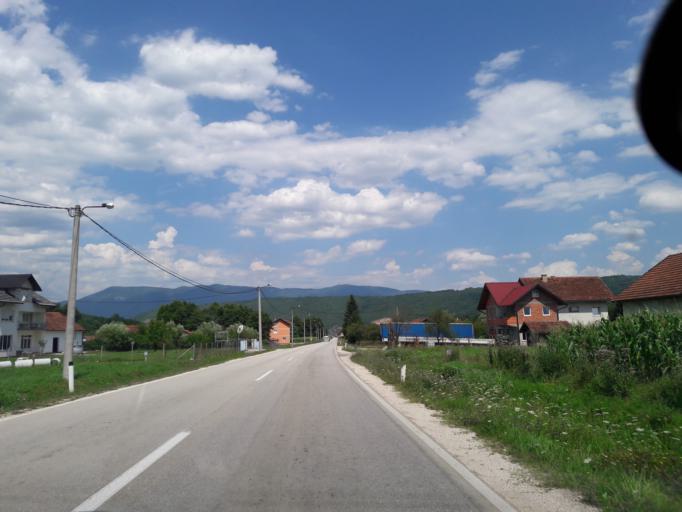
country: BA
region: Republika Srpska
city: Mrkonjic Grad
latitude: 44.4300
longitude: 17.1382
